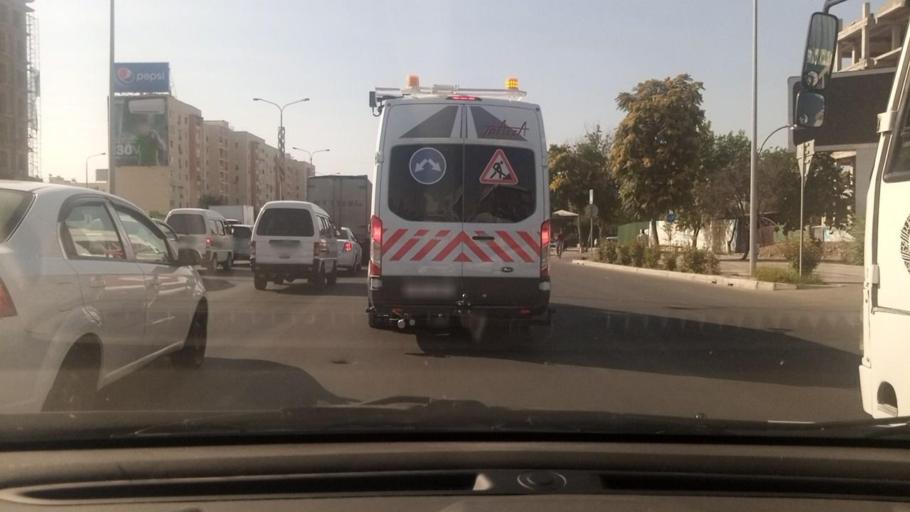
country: UZ
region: Toshkent Shahri
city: Bektemir
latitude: 41.2418
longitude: 69.3284
